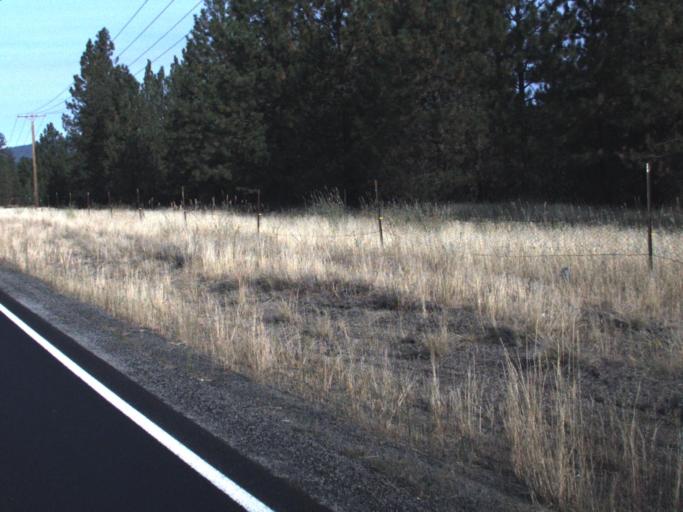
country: US
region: Washington
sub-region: Spokane County
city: Deer Park
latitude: 47.8500
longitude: -117.6372
